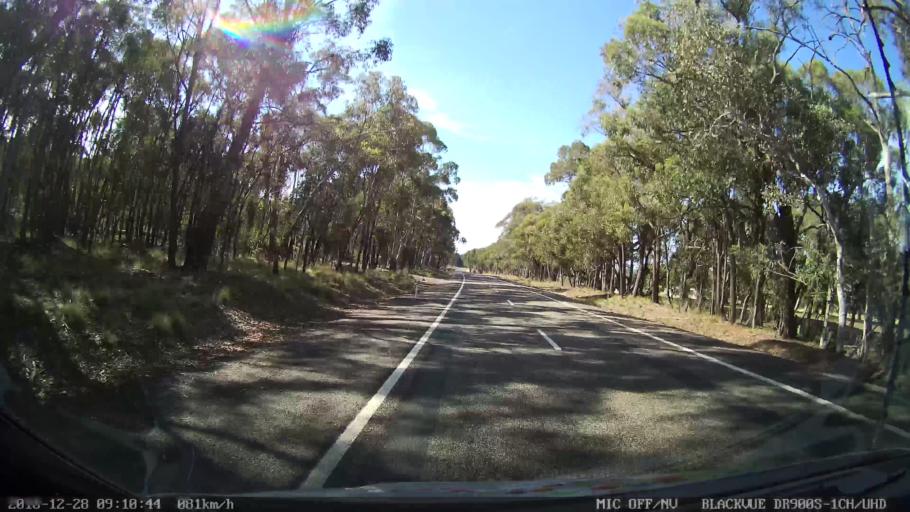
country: AU
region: New South Wales
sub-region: Upper Lachlan Shire
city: Crookwell
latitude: -34.2354
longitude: 149.3371
